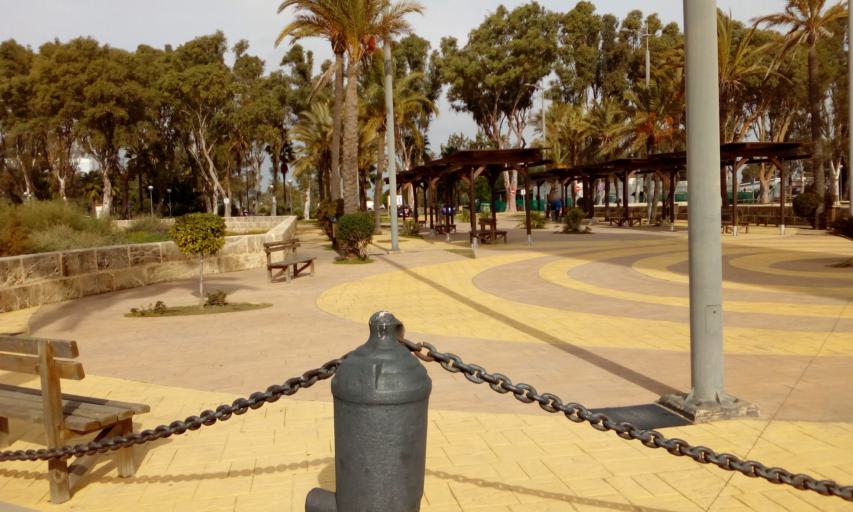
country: ES
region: Andalusia
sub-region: Provincia de Huelva
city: Punta Umbria
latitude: 37.2125
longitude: -6.9405
